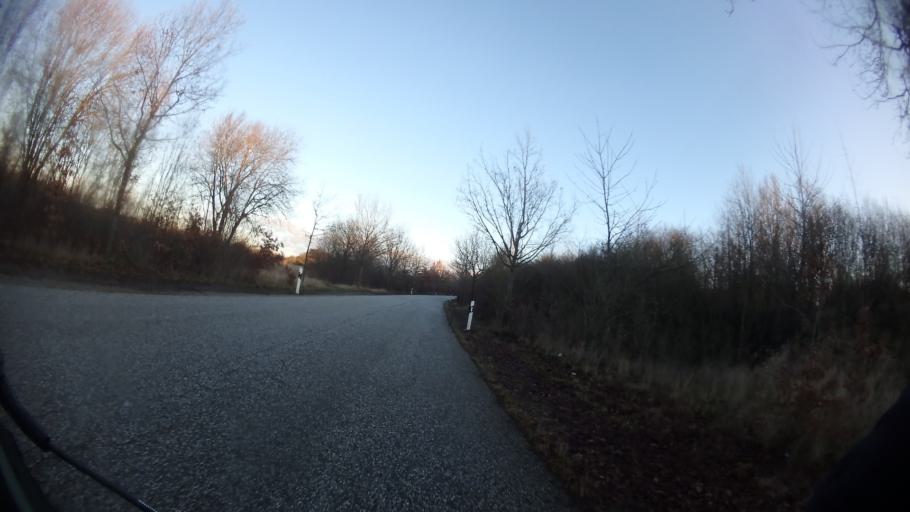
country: DE
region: Mecklenburg-Vorpommern
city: Selmsdorf
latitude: 53.9261
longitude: 10.8254
